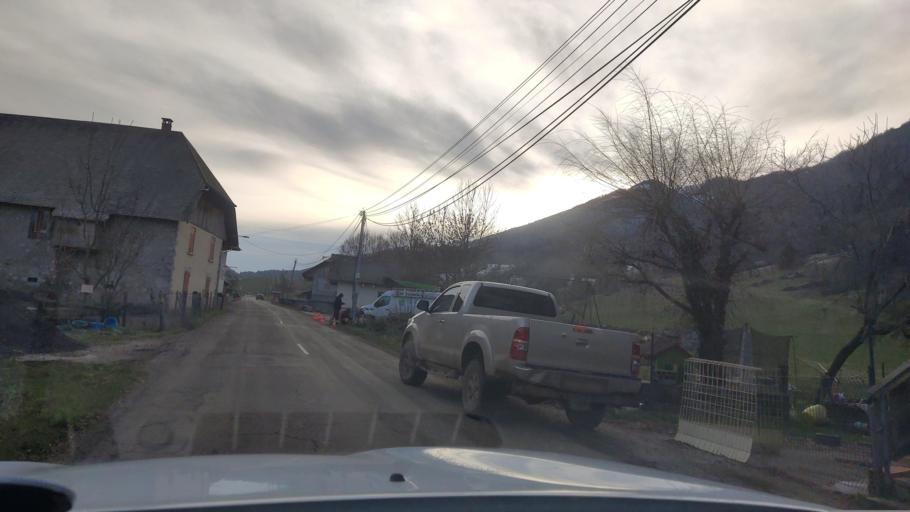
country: FR
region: Rhone-Alpes
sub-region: Departement de la Savoie
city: Coise-Saint-Jean-Pied-Gauthier
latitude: 45.6168
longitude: 6.1437
